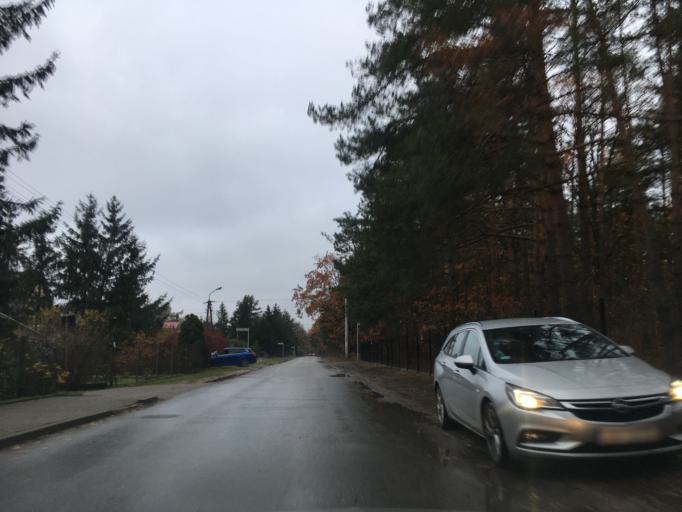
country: PL
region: Masovian Voivodeship
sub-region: Powiat piaseczynski
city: Lesznowola
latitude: 52.0913
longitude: 20.8907
